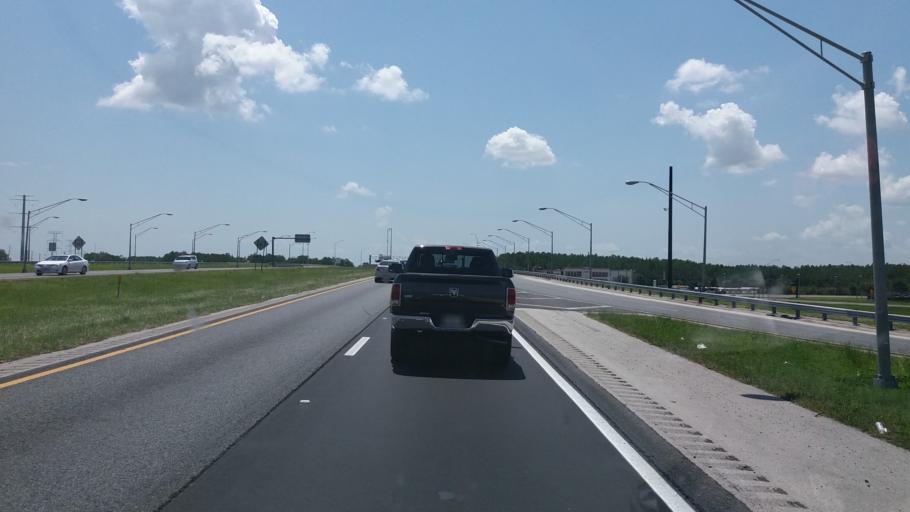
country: US
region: Florida
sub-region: Orange County
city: Hunters Creek
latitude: 28.3735
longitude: -81.4071
